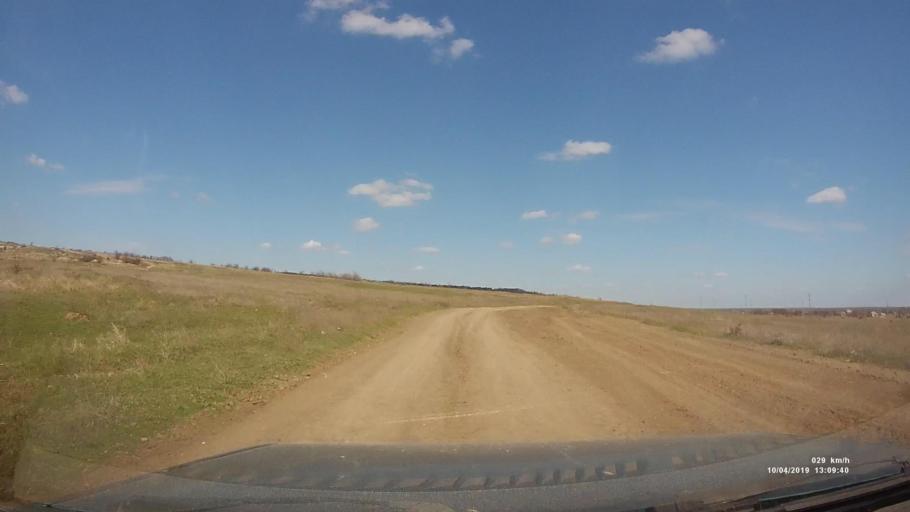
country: RU
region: Rostov
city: Masalovka
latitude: 48.4070
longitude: 40.2440
